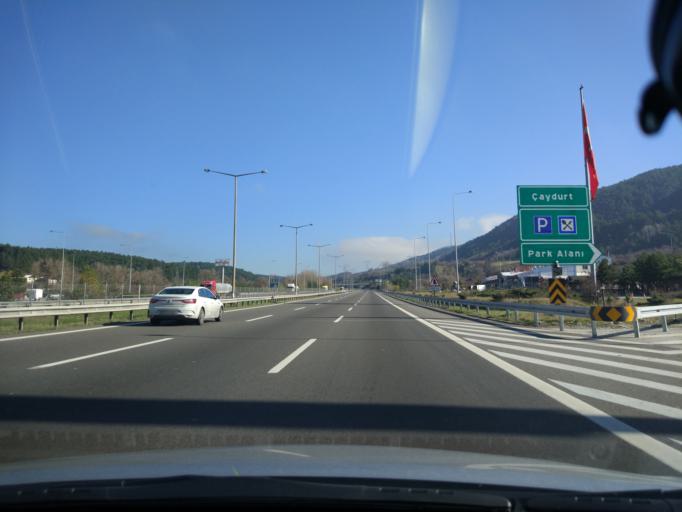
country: TR
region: Bolu
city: Yenicaga
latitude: 40.7429
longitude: 31.8582
